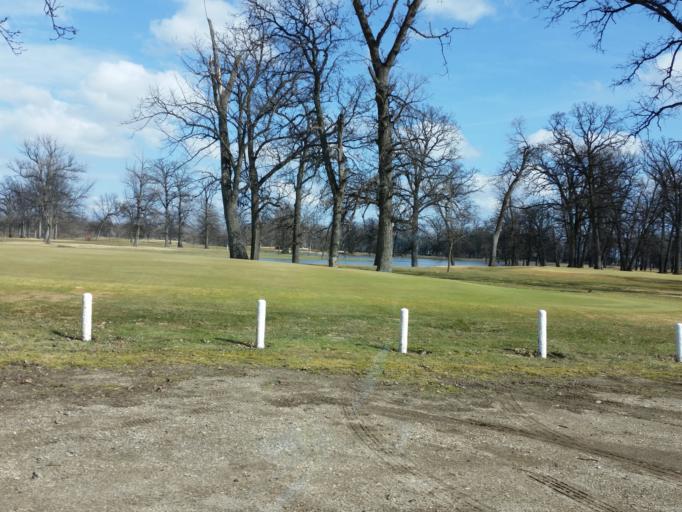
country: US
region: North Dakota
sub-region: Walsh County
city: Grafton
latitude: 48.4224
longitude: -97.3916
